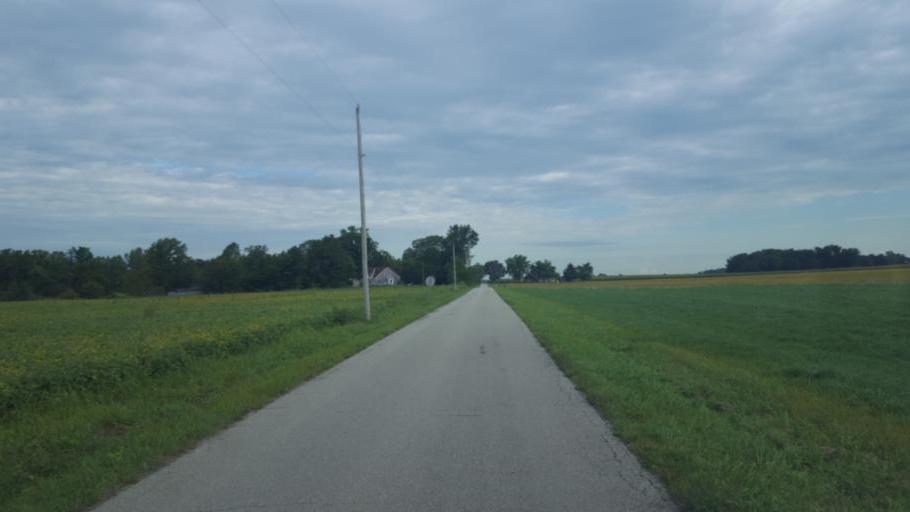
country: US
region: Ohio
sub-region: Crawford County
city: Bucyrus
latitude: 40.7211
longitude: -83.0379
